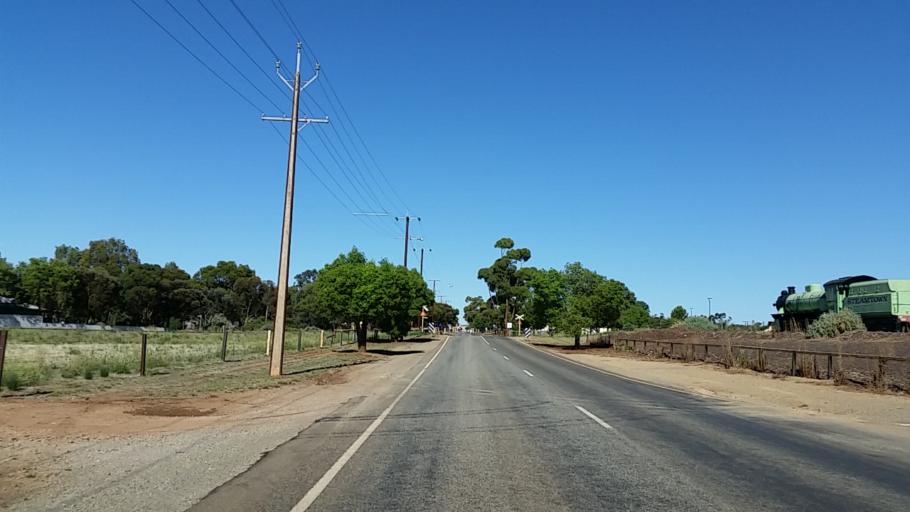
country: AU
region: South Australia
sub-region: Peterborough
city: Peterborough
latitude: -32.9743
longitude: 138.8277
